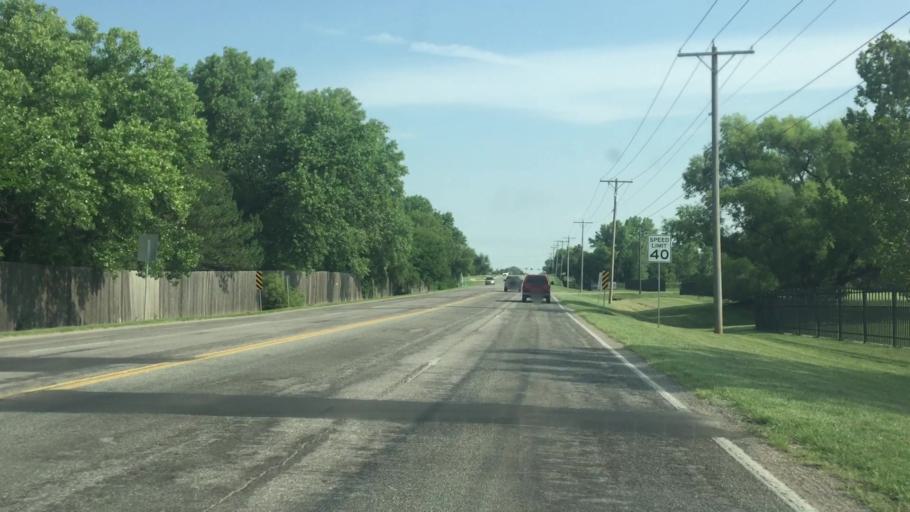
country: US
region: Kansas
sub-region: Sedgwick County
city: Bellaire
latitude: 37.7026
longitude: -97.2262
